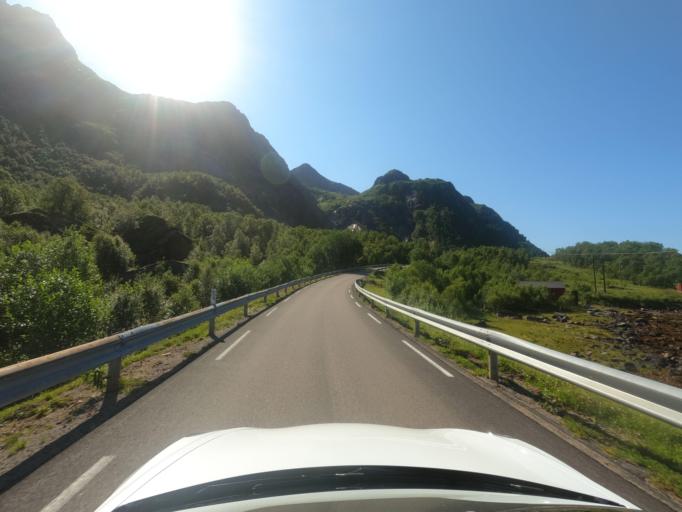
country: NO
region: Nordland
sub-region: Hadsel
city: Stokmarknes
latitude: 68.3433
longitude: 15.0510
